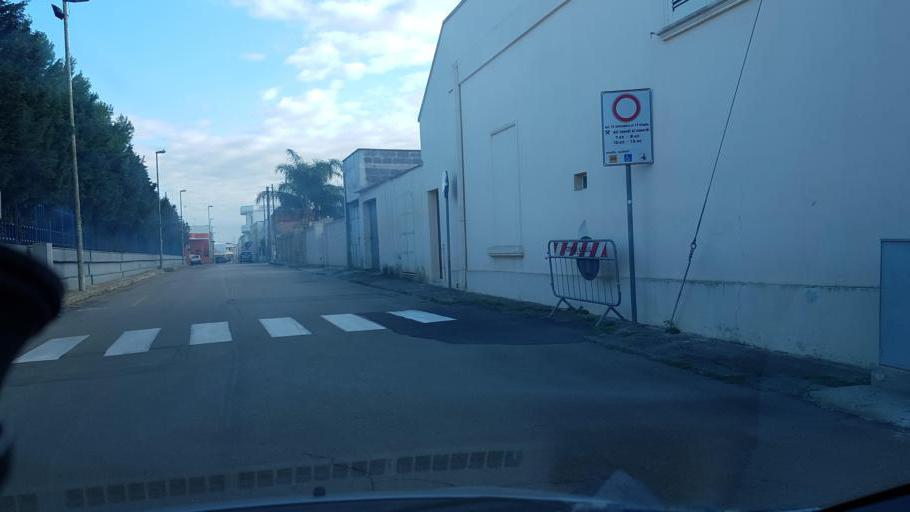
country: IT
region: Apulia
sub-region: Provincia di Lecce
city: Veglie
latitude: 40.3380
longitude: 17.9710
